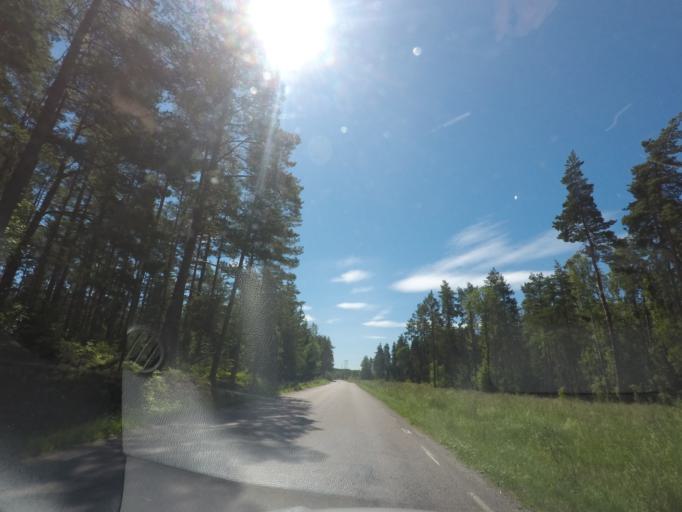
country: SE
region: Uppsala
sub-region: Enkopings Kommun
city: Irsta
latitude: 59.6728
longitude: 16.8381
